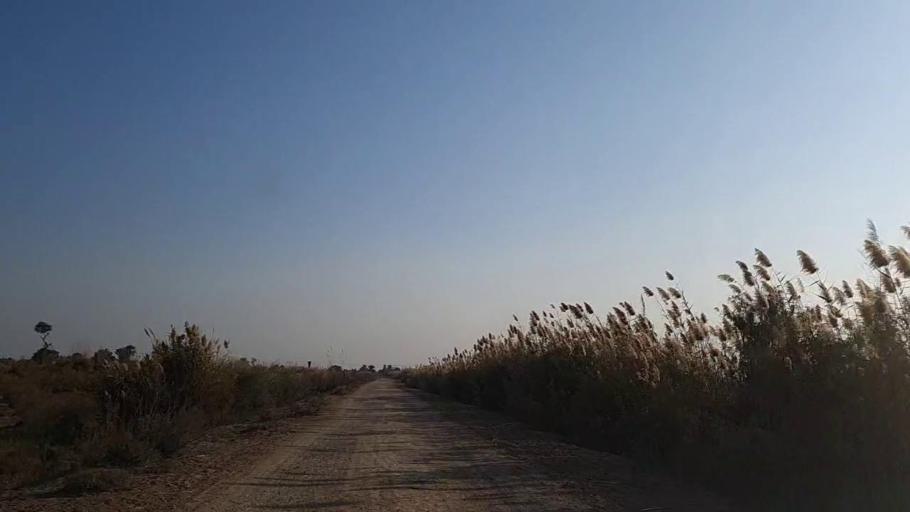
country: PK
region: Sindh
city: Daur
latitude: 26.4214
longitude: 68.3547
